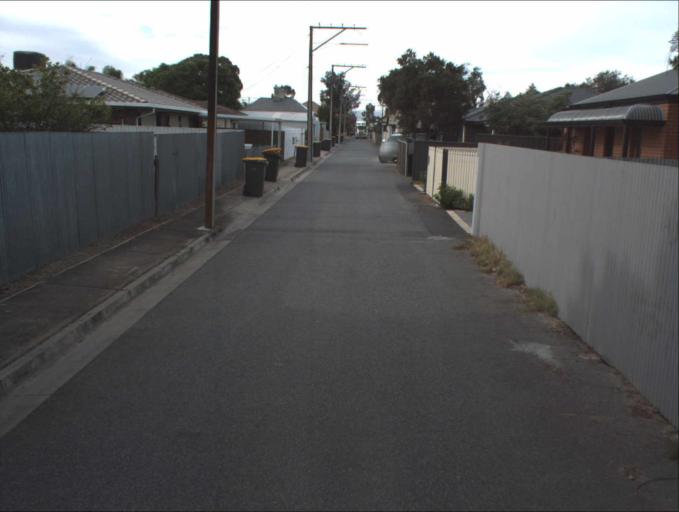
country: AU
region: South Australia
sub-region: Port Adelaide Enfield
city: Birkenhead
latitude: -34.8340
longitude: 138.4963
